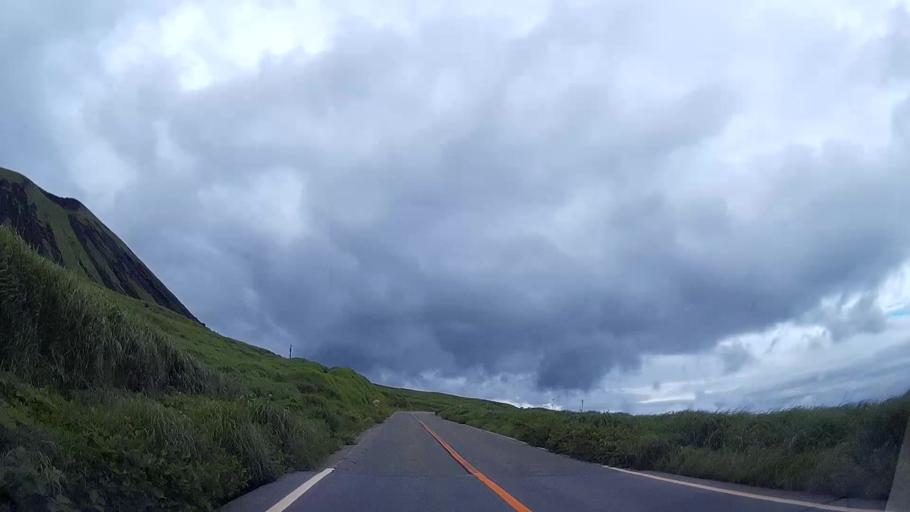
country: JP
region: Kumamoto
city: Aso
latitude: 32.9046
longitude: 131.0548
